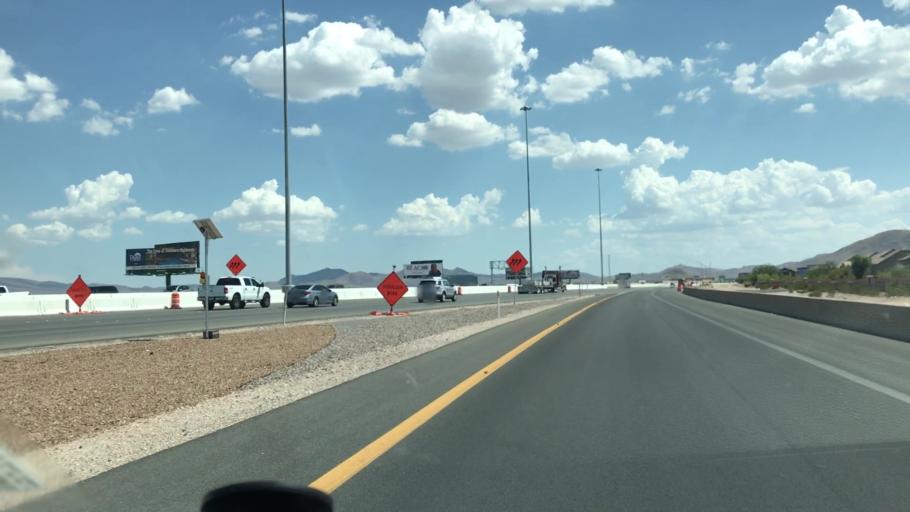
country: US
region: Nevada
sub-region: Clark County
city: Enterprise
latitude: 35.9963
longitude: -115.1811
